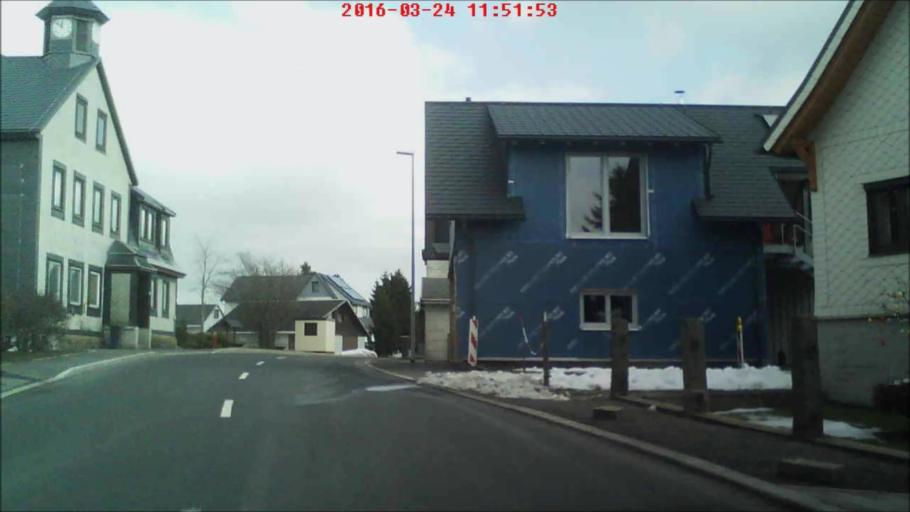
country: DE
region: Thuringia
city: Steinheid
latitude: 50.4714
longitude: 11.0522
